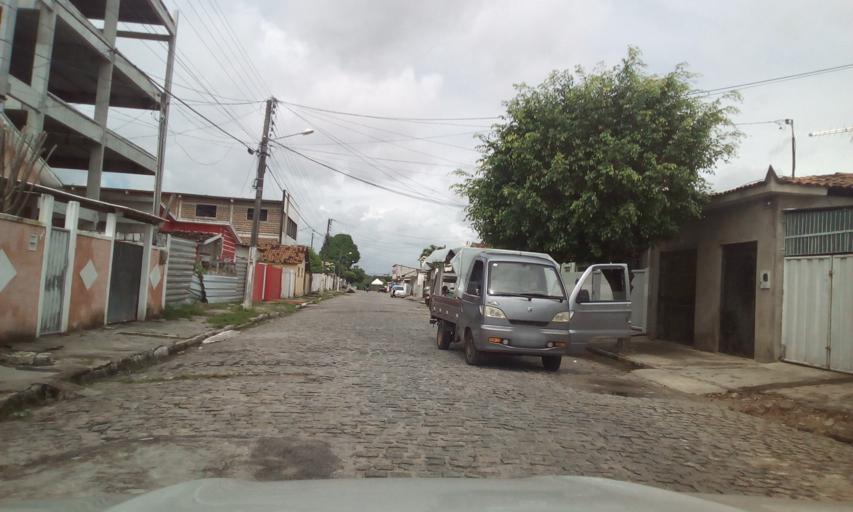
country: BR
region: Paraiba
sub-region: Bayeux
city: Bayeux
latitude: -7.1228
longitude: -34.9066
